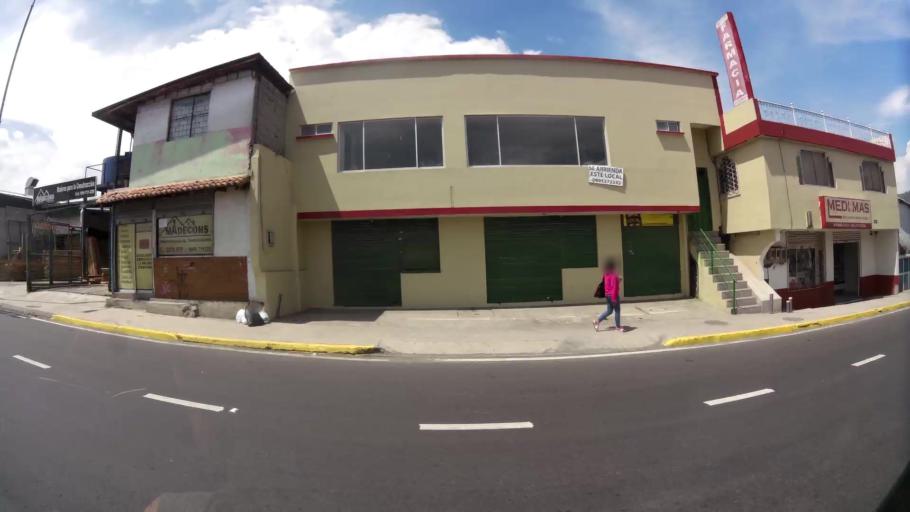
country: EC
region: Pichincha
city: Sangolqui
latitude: -0.2104
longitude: -78.3859
